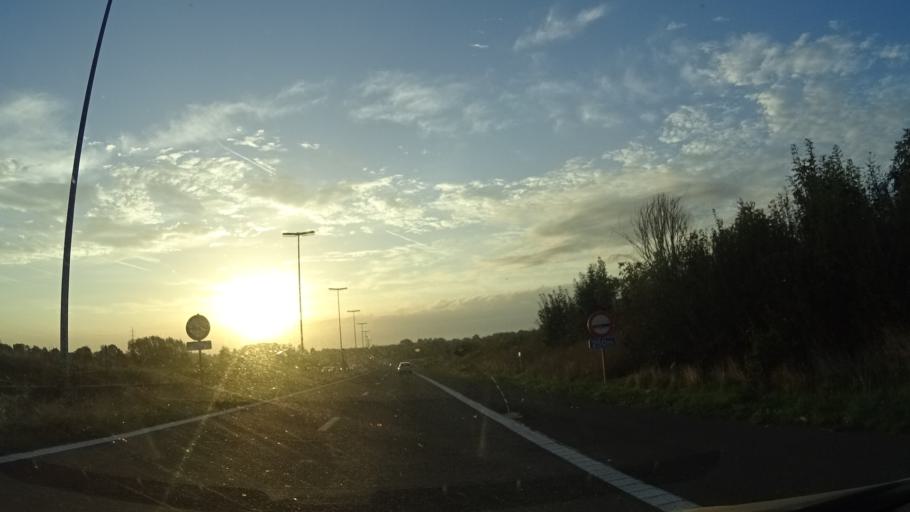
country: BE
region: Wallonia
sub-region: Province du Hainaut
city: Chasse Royale
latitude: 50.4072
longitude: 3.9504
